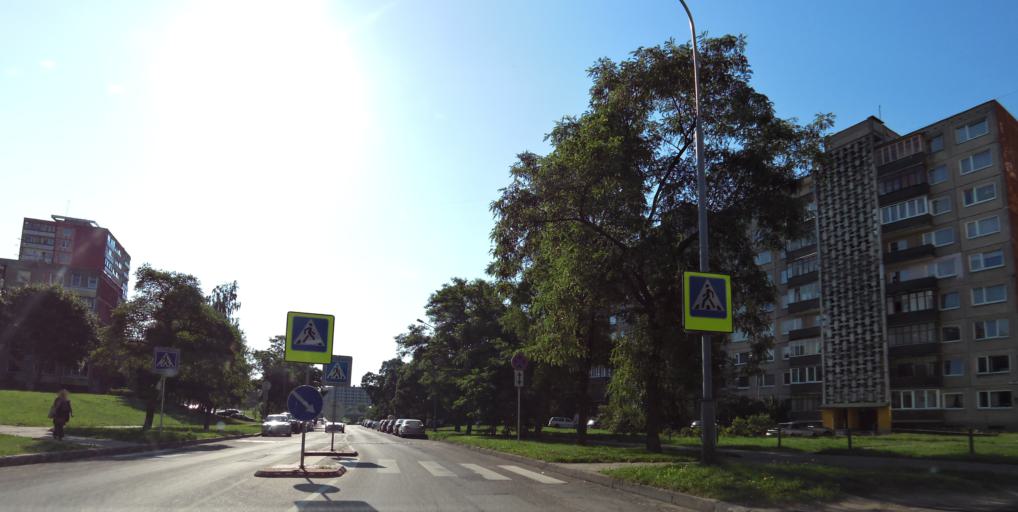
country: LT
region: Vilnius County
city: Justiniskes
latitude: 54.6957
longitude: 25.2143
